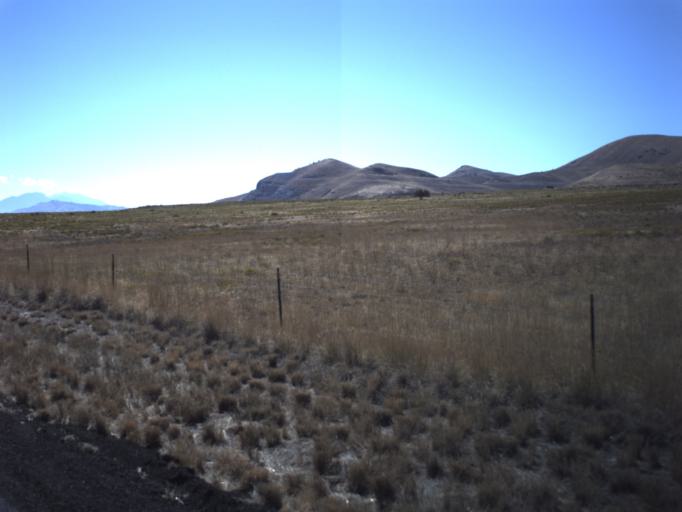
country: US
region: Utah
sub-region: Utah County
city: Saratoga Springs
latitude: 40.2807
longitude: -111.8714
